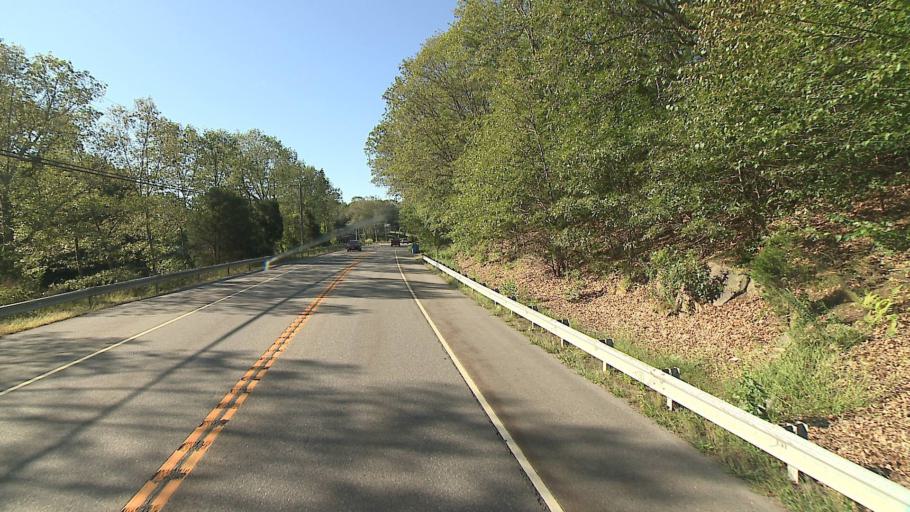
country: US
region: Connecticut
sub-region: New London County
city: Gales Ferry
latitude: 41.4360
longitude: -72.0799
